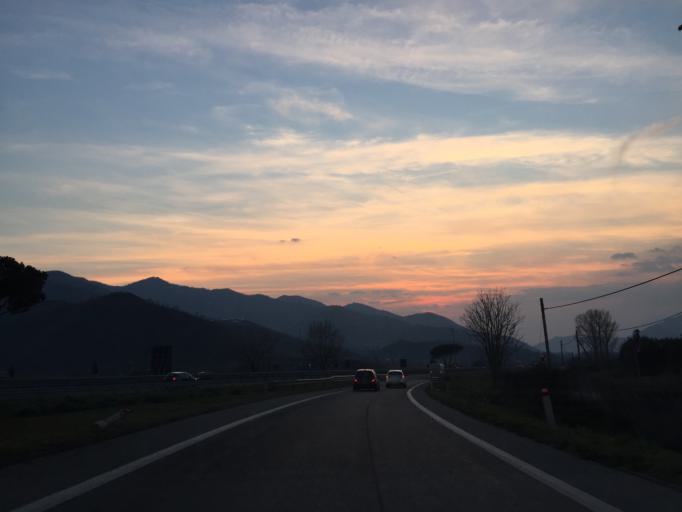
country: IT
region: Campania
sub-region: Provincia di Salerno
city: Lancusi-Penta-Bolano
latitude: 40.7724
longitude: 14.7815
